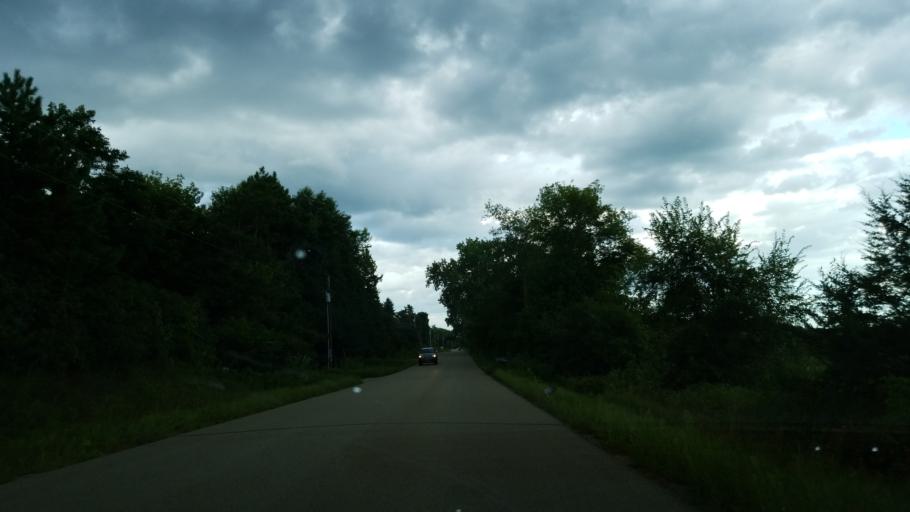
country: US
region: Minnesota
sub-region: Washington County
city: Lake Saint Croix Beach
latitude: 44.8802
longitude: -92.7404
